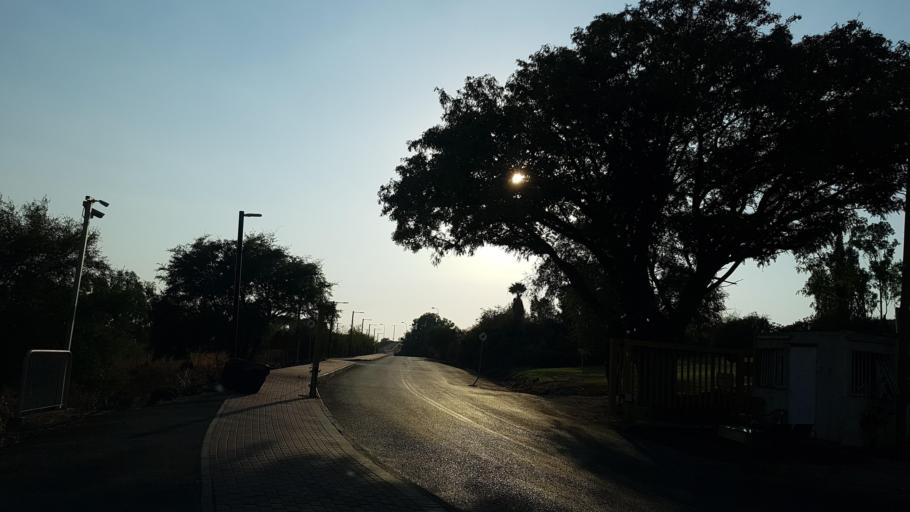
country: SY
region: Quneitra
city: Al Butayhah
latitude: 32.9136
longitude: 35.5990
